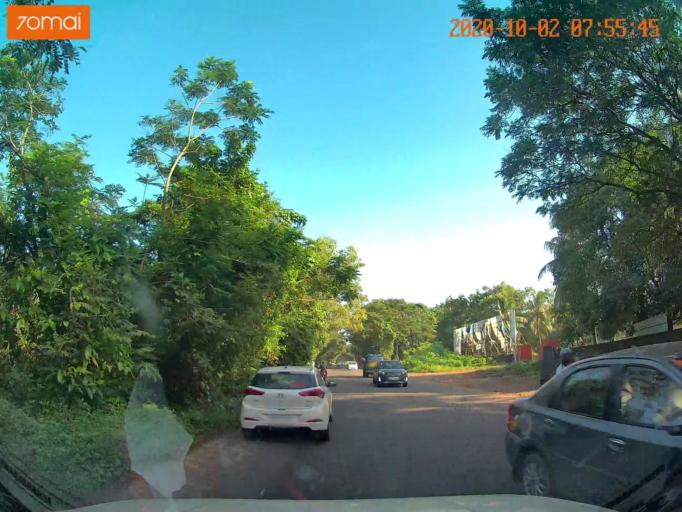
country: IN
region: Kerala
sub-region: Kozhikode
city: Ferokh
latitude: 11.1852
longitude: 75.8710
